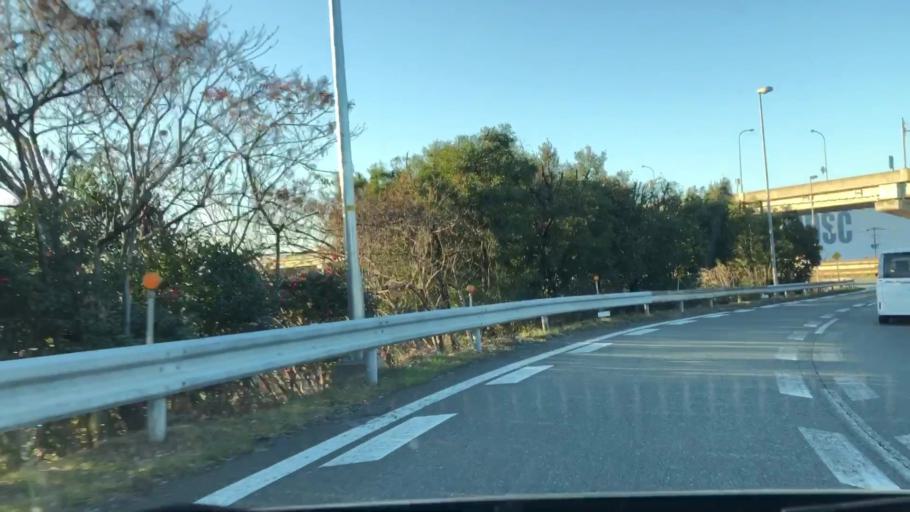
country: JP
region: Fukuoka
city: Umi
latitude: 33.6285
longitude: 130.4829
